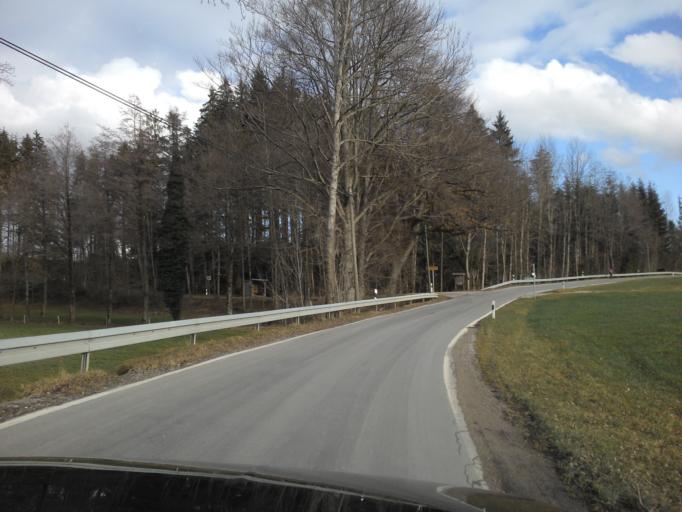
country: DE
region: Bavaria
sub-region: Upper Bavaria
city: Kreut
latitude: 47.7710
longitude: 11.5031
